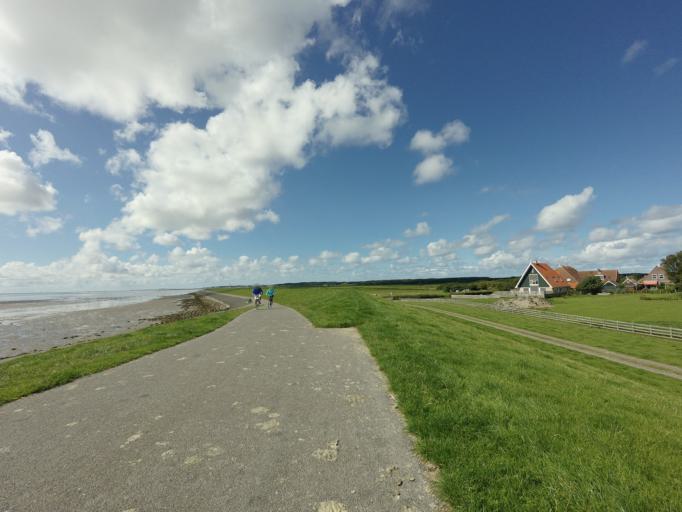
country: NL
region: Friesland
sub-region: Gemeente Terschelling
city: West-Terschelling
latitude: 53.3737
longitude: 5.2757
